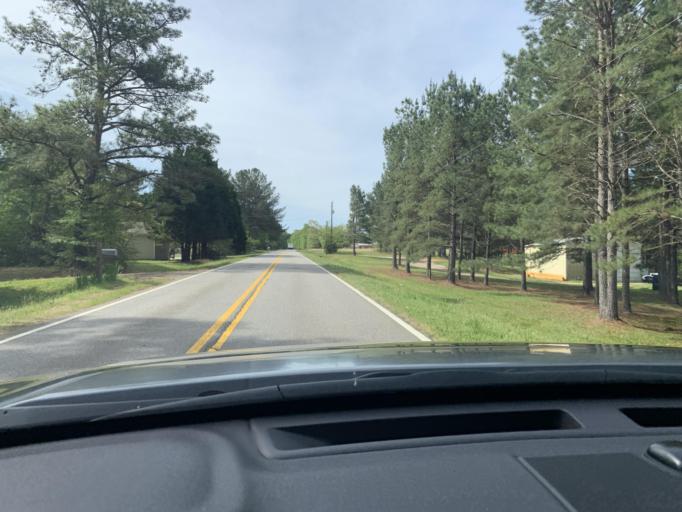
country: US
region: Georgia
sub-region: Oconee County
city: Watkinsville
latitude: 33.8317
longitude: -83.5063
